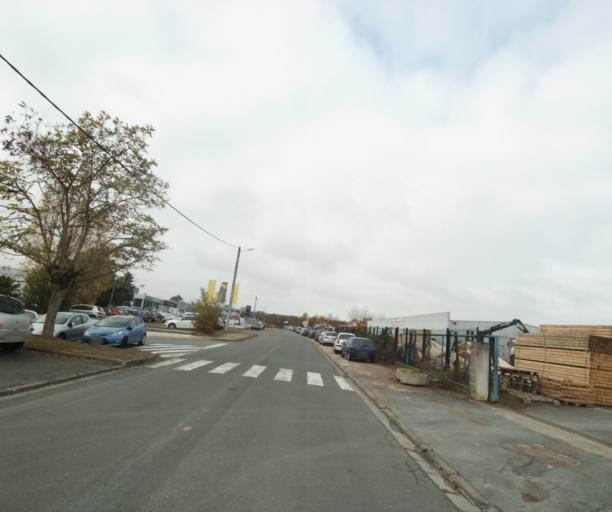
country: FR
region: Poitou-Charentes
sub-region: Departement de la Charente-Maritime
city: Saintes
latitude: 45.7432
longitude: -0.6661
